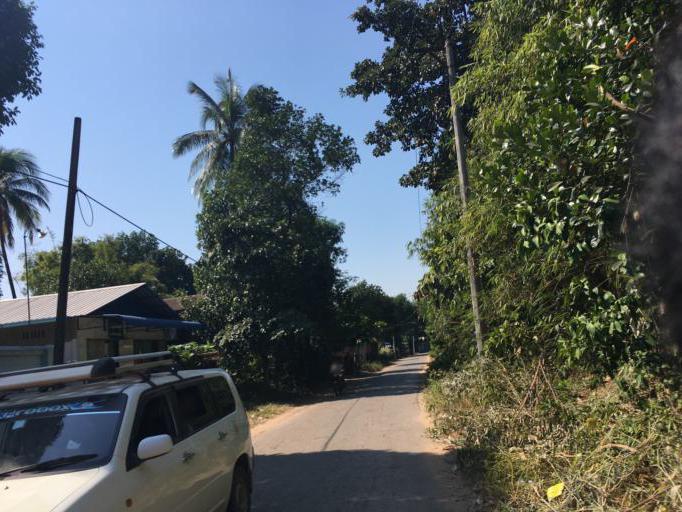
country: MM
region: Mon
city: Mawlamyine
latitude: 16.4340
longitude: 97.6992
